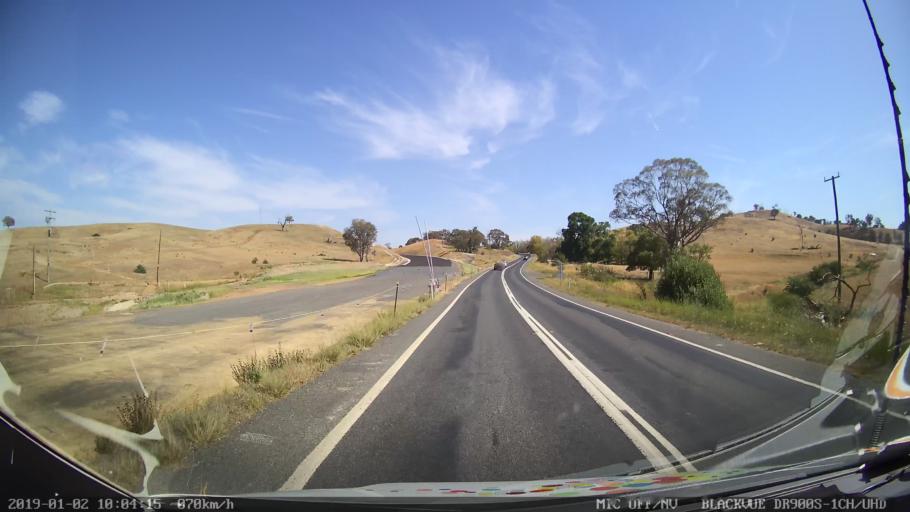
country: AU
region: New South Wales
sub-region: Gundagai
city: Gundagai
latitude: -35.1696
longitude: 148.1235
